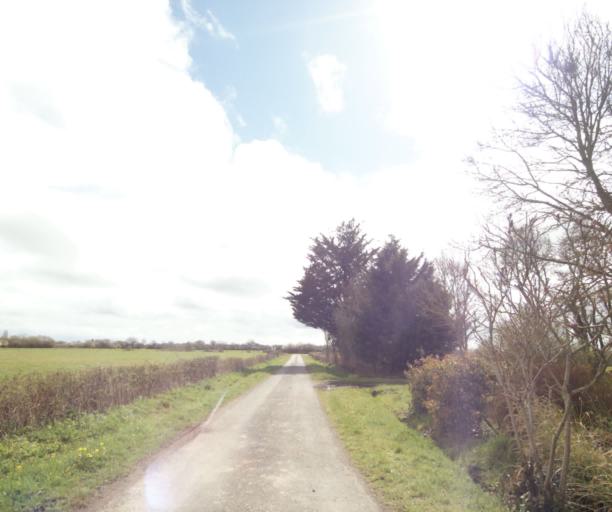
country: FR
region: Pays de la Loire
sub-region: Departement de la Loire-Atlantique
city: Bouvron
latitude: 47.4236
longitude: -1.8845
